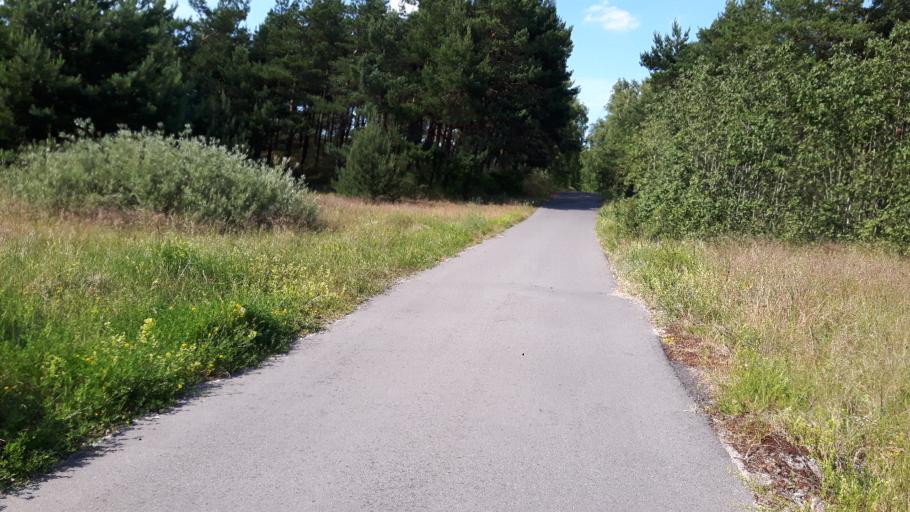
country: LT
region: Klaipedos apskritis
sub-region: Klaipeda
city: Klaipeda
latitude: 55.6858
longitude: 21.1039
